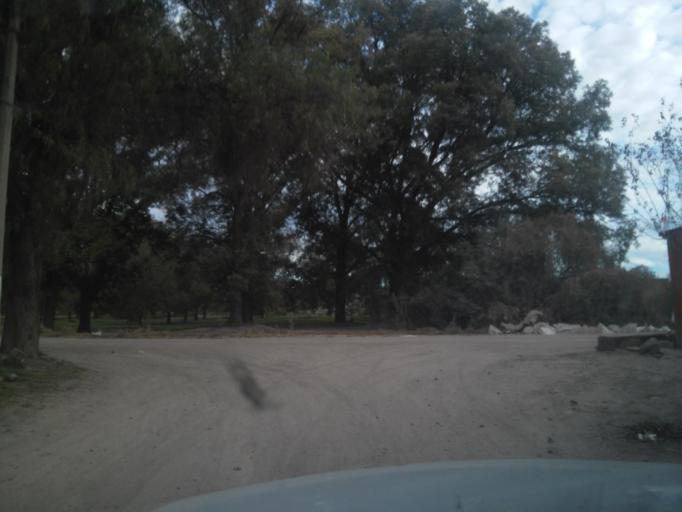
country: MX
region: Durango
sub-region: Durango
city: Jose Refugio Salcido
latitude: 24.0481
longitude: -104.5488
